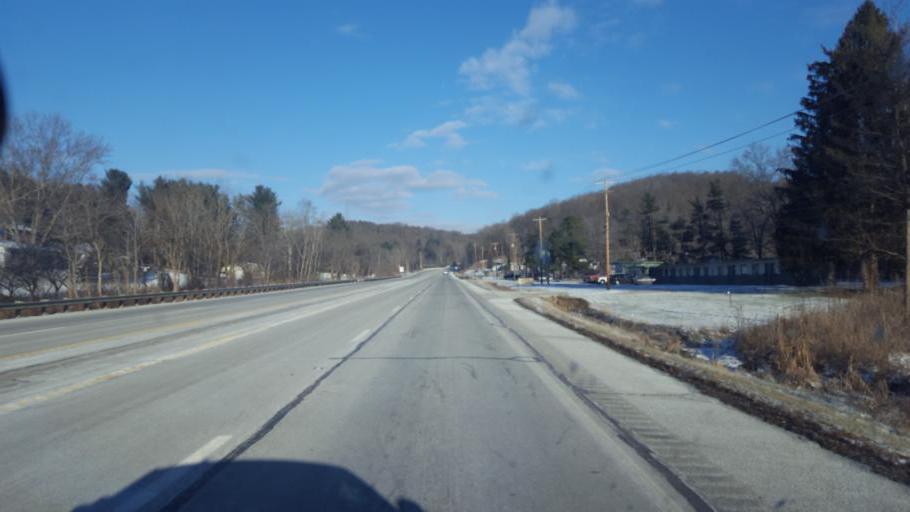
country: US
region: Ohio
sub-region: Pike County
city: Waverly
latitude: 39.2015
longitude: -82.9802
